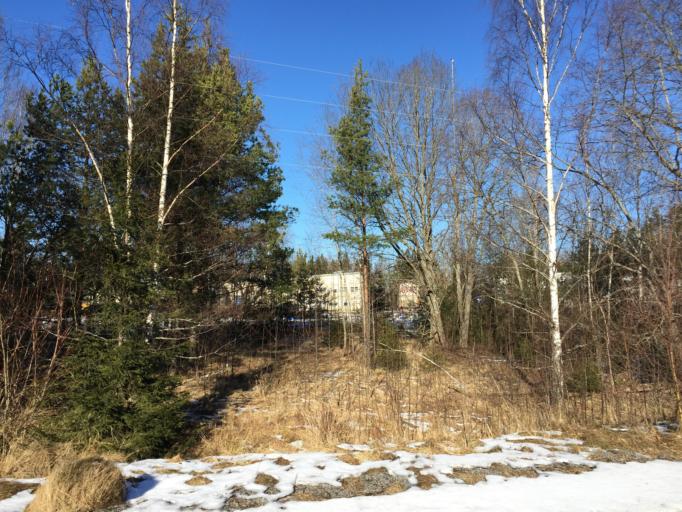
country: SE
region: Stockholm
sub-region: Nykvarns Kommun
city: Nykvarn
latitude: 59.1660
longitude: 17.5300
